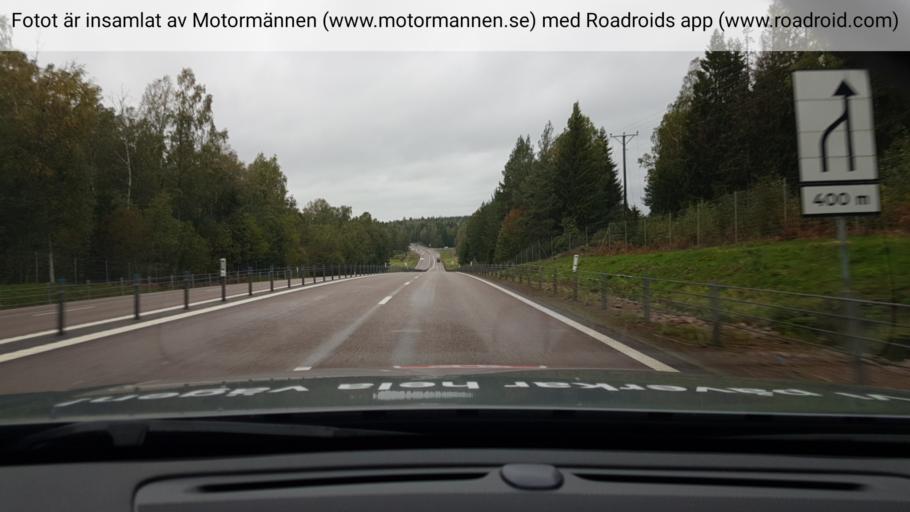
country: SE
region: Vaermland
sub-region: Kristinehamns Kommun
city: Kristinehamn
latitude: 59.3446
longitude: 14.0858
